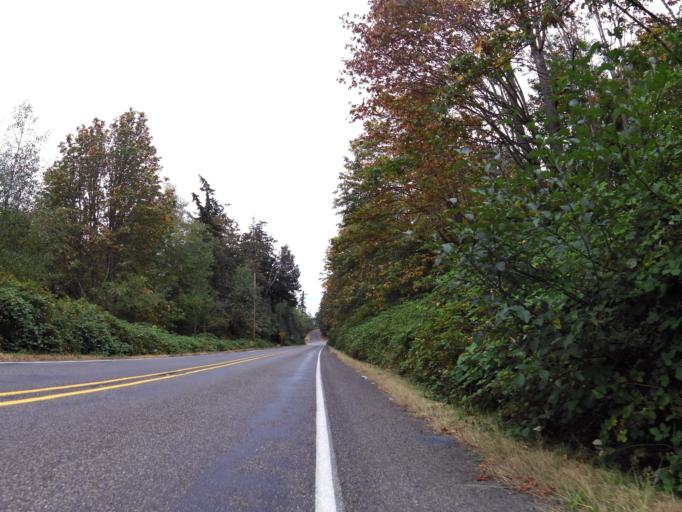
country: US
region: Washington
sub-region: Kitsap County
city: Lofall
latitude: 47.8701
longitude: -122.6370
